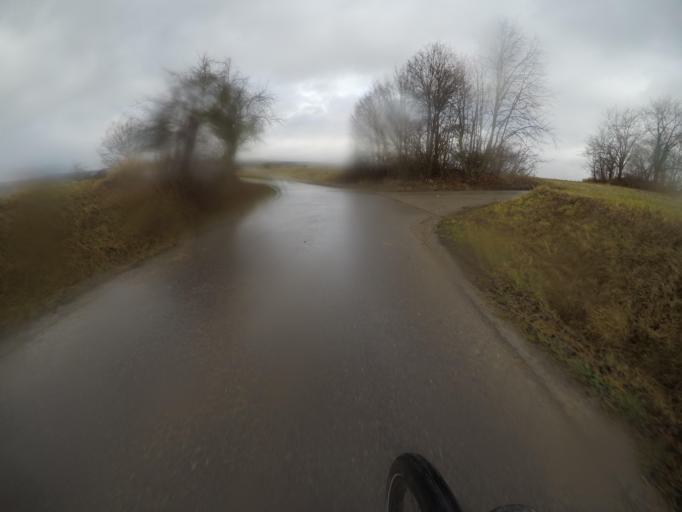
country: DE
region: Baden-Wuerttemberg
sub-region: Regierungsbezirk Stuttgart
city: Eberdingen
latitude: 48.9039
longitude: 8.9969
